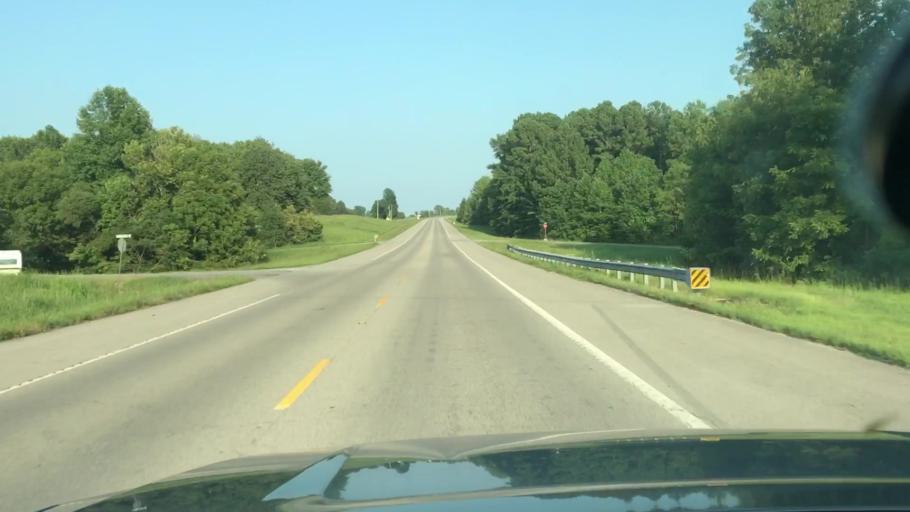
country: US
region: Tennessee
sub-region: Sumner County
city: Portland
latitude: 36.5776
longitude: -86.4033
